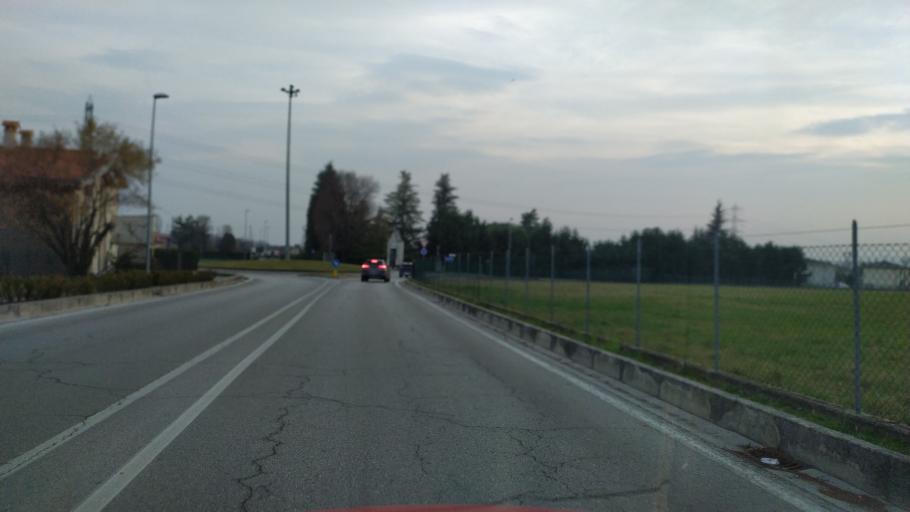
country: IT
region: Veneto
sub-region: Provincia di Vicenza
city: Montecchio Precalcino
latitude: 45.6592
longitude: 11.5582
